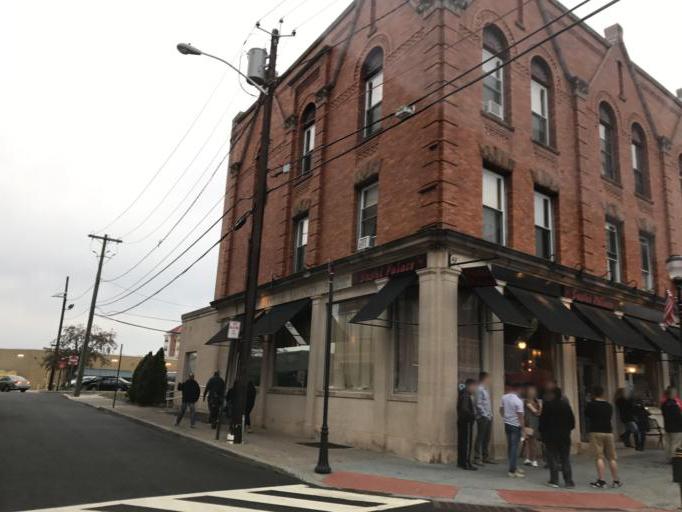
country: US
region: New Jersey
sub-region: Somerset County
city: Somerville
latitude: 40.5671
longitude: -74.6134
